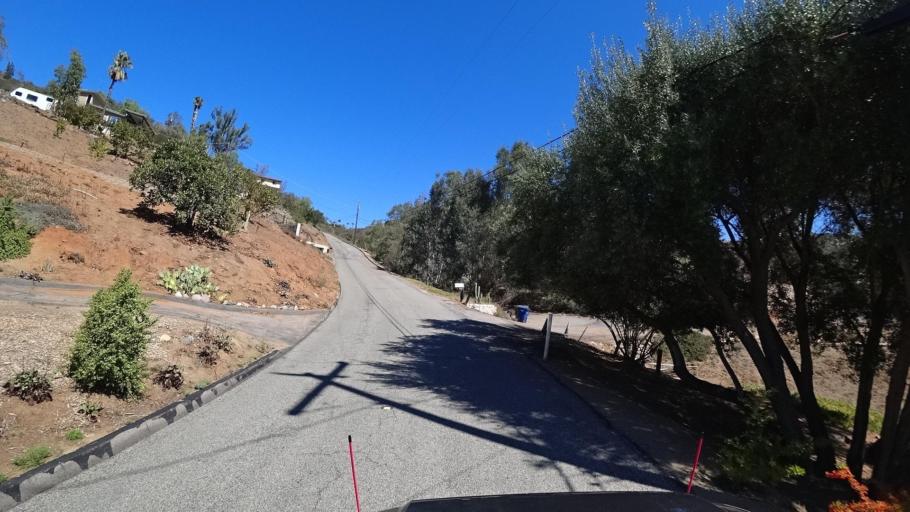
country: US
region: California
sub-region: San Diego County
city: Jamul
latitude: 32.7353
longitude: -116.8822
